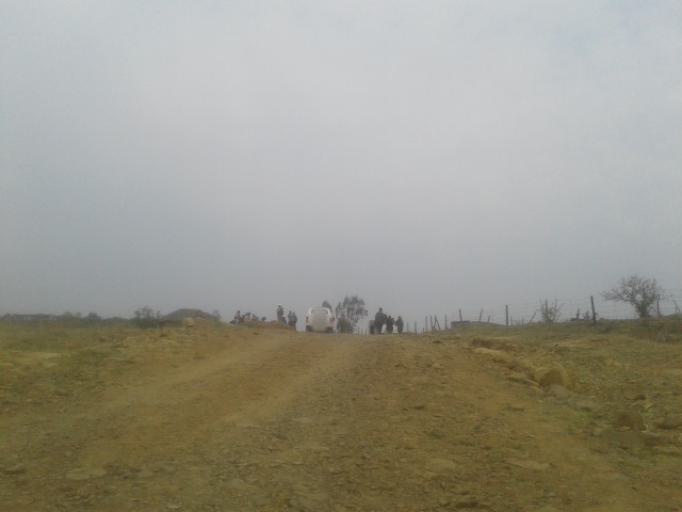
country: LS
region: Berea
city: Teyateyaneng
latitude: -29.0861
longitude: 27.9059
